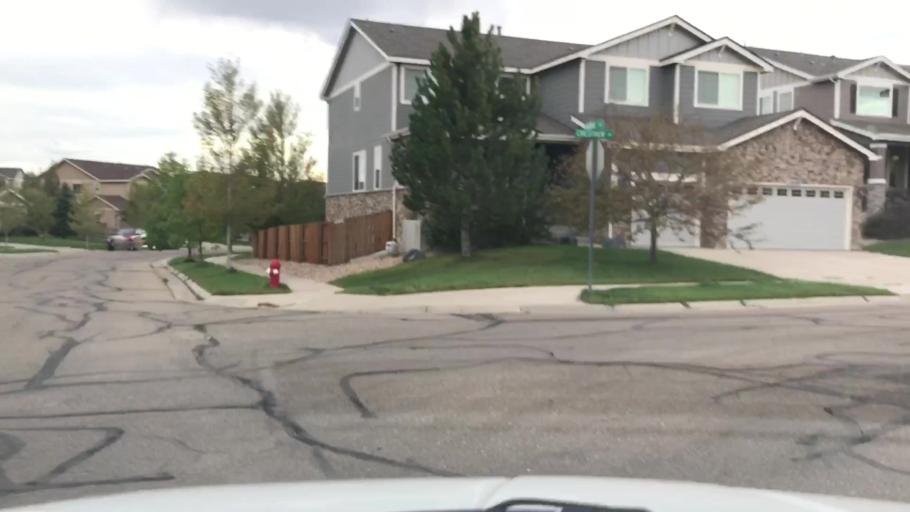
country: US
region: Colorado
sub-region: Boulder County
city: Erie
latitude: 40.0140
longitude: -105.0204
